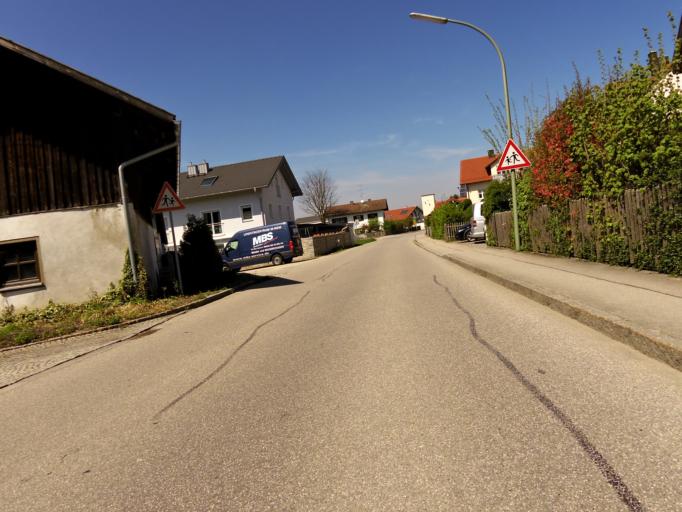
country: DE
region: Bavaria
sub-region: Upper Bavaria
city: Walpertskirchen
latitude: 48.2629
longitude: 11.9718
